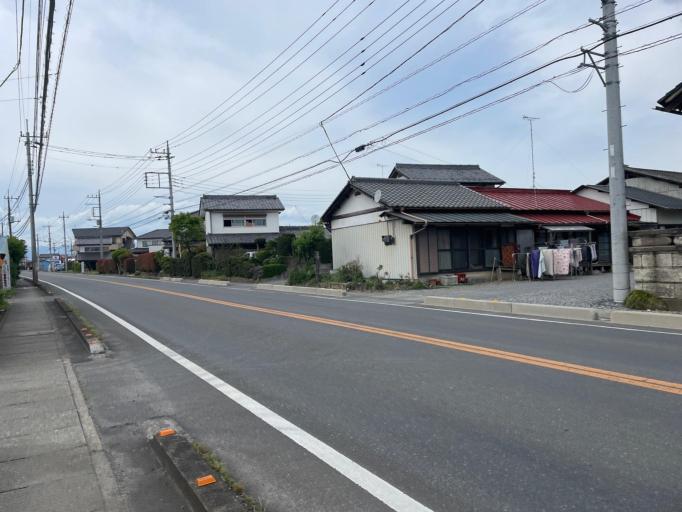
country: JP
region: Tochigi
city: Mibu
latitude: 36.4568
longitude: 139.7737
